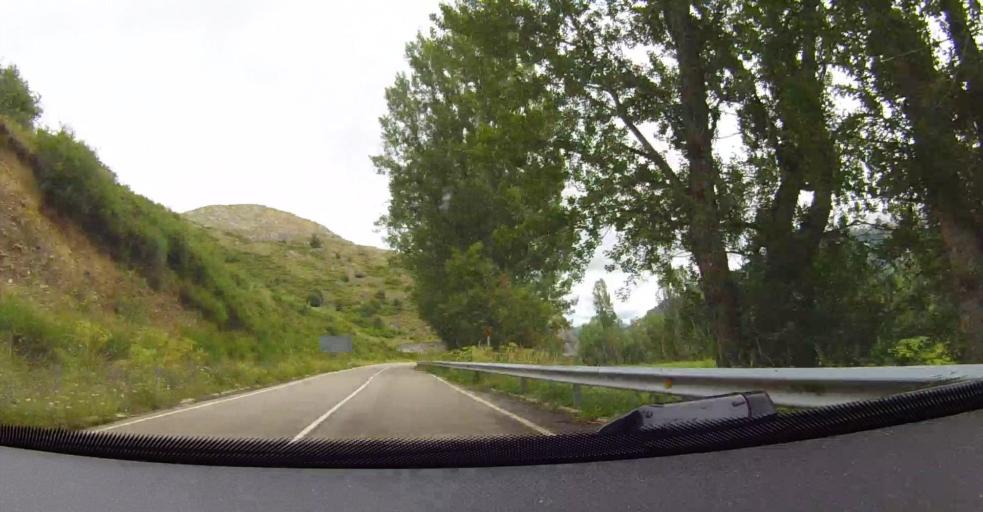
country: ES
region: Castille and Leon
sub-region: Provincia de Leon
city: Buron
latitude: 43.0283
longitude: -5.0665
